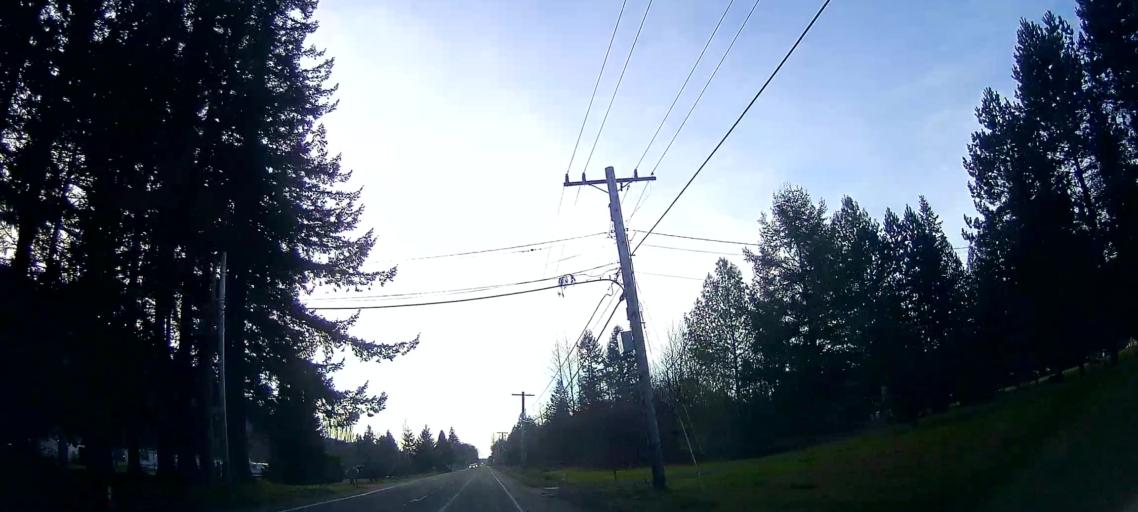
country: US
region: Washington
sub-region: Skagit County
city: Sedro-Woolley
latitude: 48.5271
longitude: -121.9248
